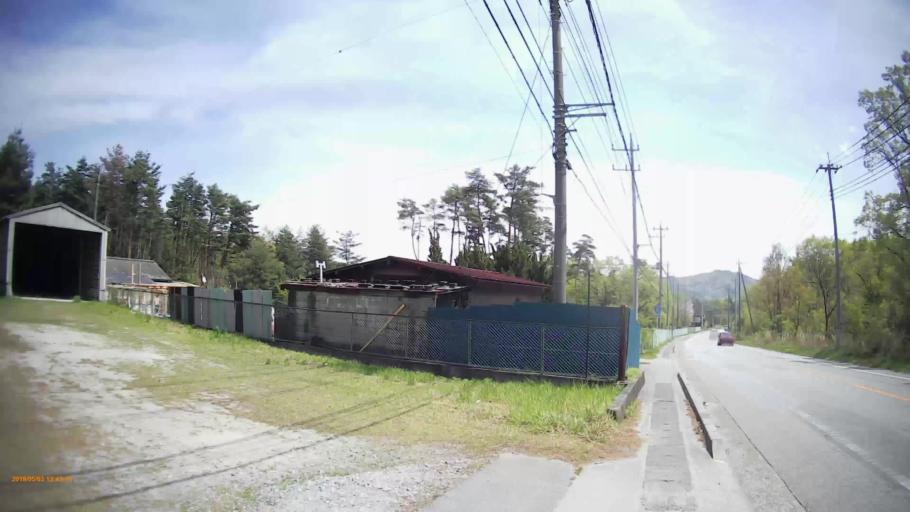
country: JP
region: Yamanashi
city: Nirasaki
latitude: 35.8398
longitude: 138.3032
